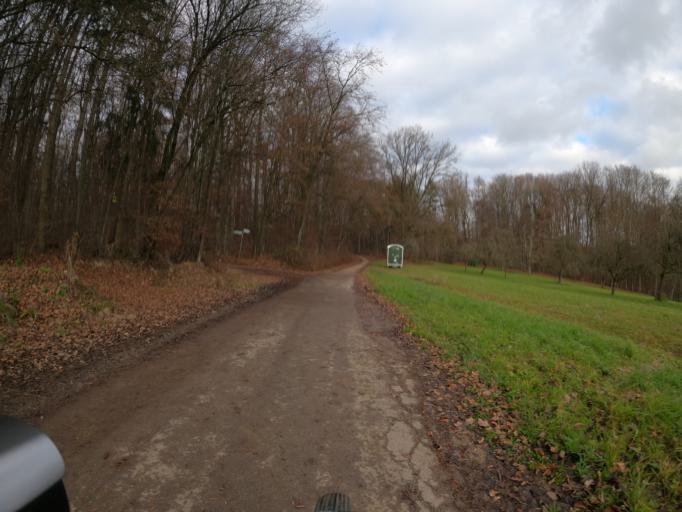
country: DE
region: Baden-Wuerttemberg
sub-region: Regierungsbezirk Stuttgart
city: Notzingen
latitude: 48.6773
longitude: 9.4674
